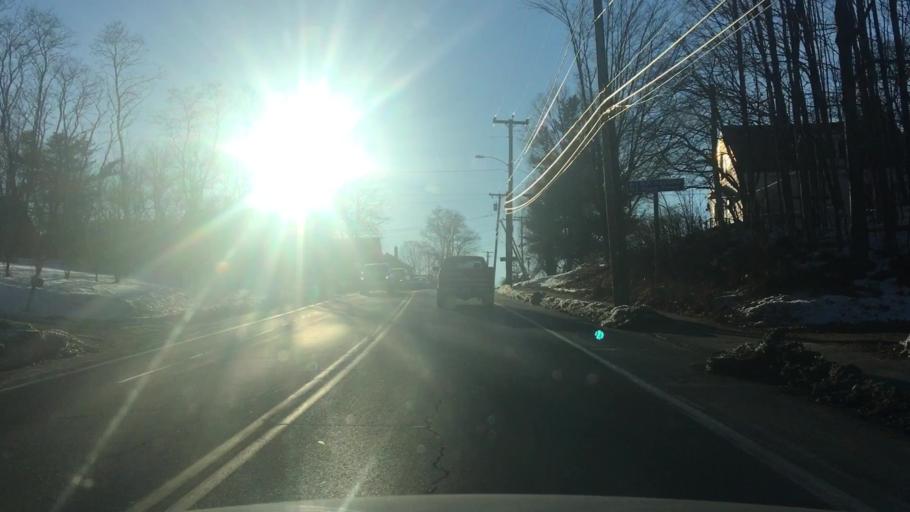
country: US
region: Maine
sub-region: Somerset County
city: Skowhegan
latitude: 44.7610
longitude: -69.7210
